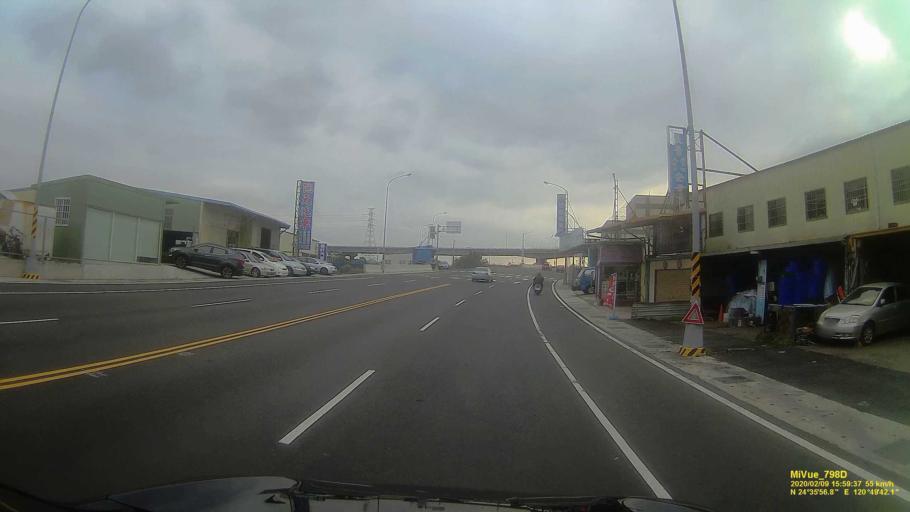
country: TW
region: Taiwan
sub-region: Miaoli
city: Miaoli
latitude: 24.5989
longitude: 120.8283
